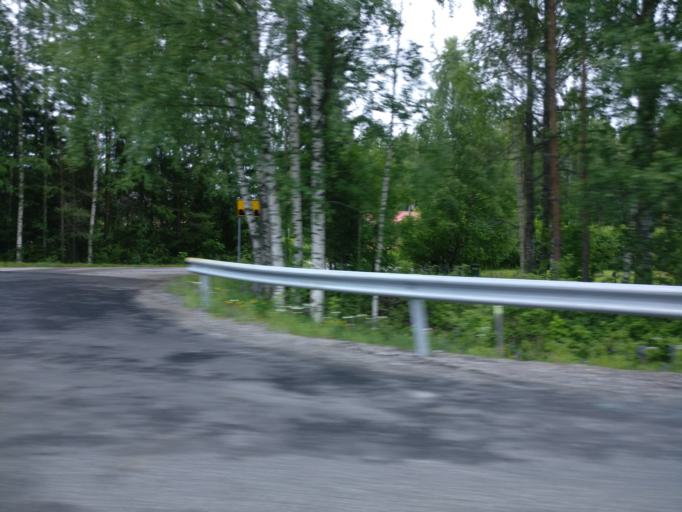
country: FI
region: Northern Savo
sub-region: Varkaus
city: Leppaevirta
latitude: 62.5890
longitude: 27.6051
